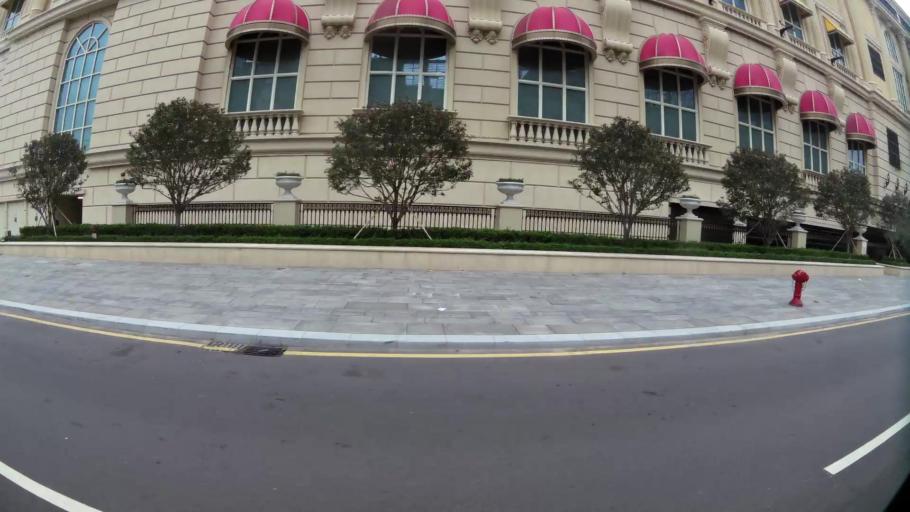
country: MO
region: Macau
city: Macau
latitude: 22.1427
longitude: 113.5611
